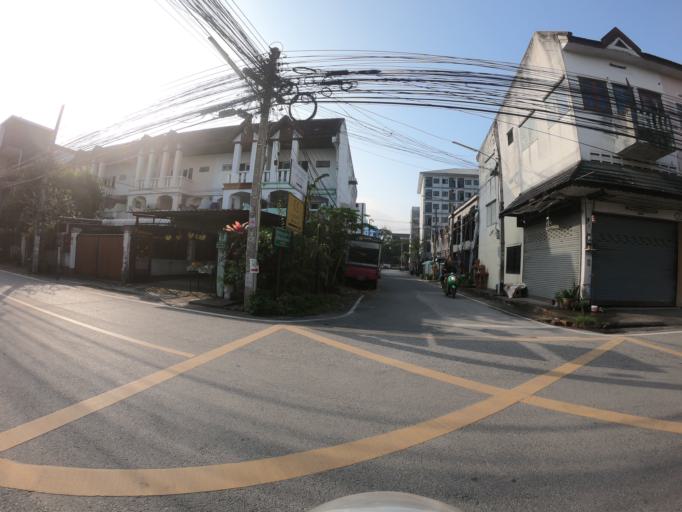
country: TH
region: Chiang Mai
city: Chiang Mai
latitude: 18.8123
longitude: 98.9660
